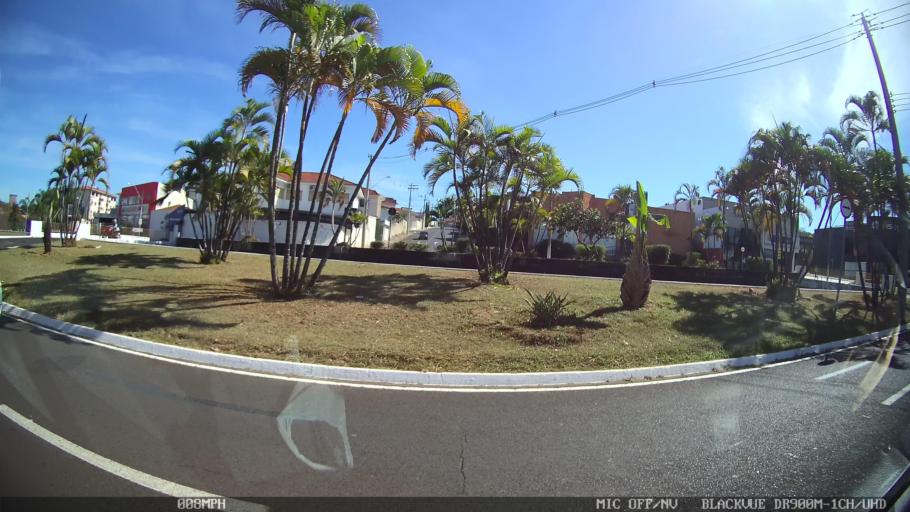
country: BR
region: Sao Paulo
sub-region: Franca
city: Franca
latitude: -20.5478
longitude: -47.4010
